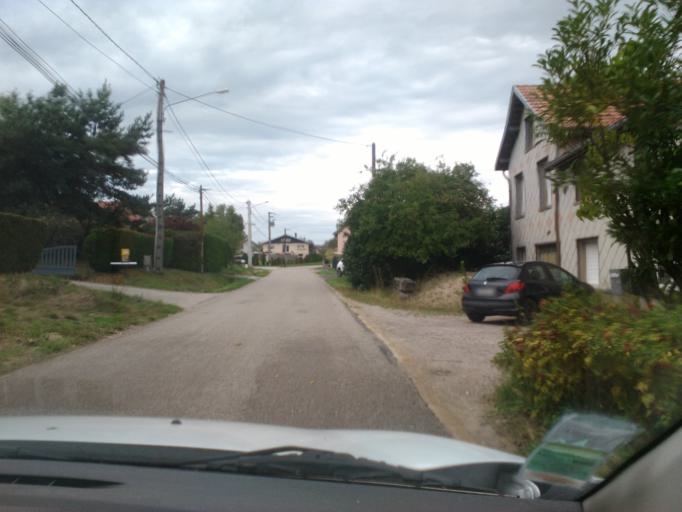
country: FR
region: Lorraine
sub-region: Departement des Vosges
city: Saint-Michel-sur-Meurthe
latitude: 48.3184
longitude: 6.8556
